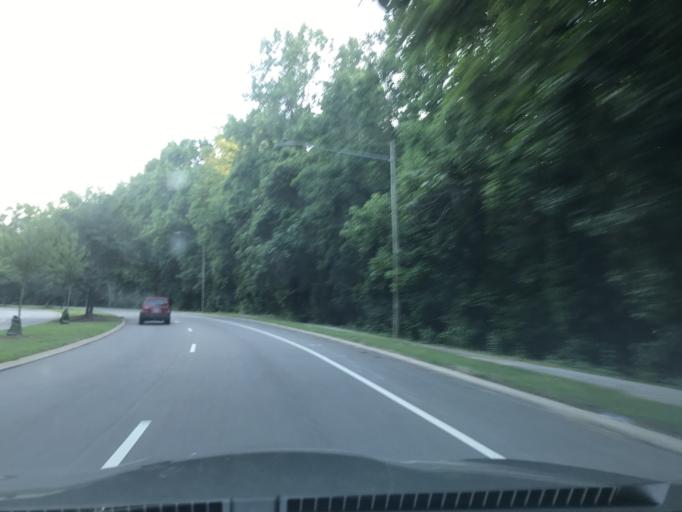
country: US
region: North Carolina
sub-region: Wake County
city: Raleigh
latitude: 35.7995
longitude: -78.6106
